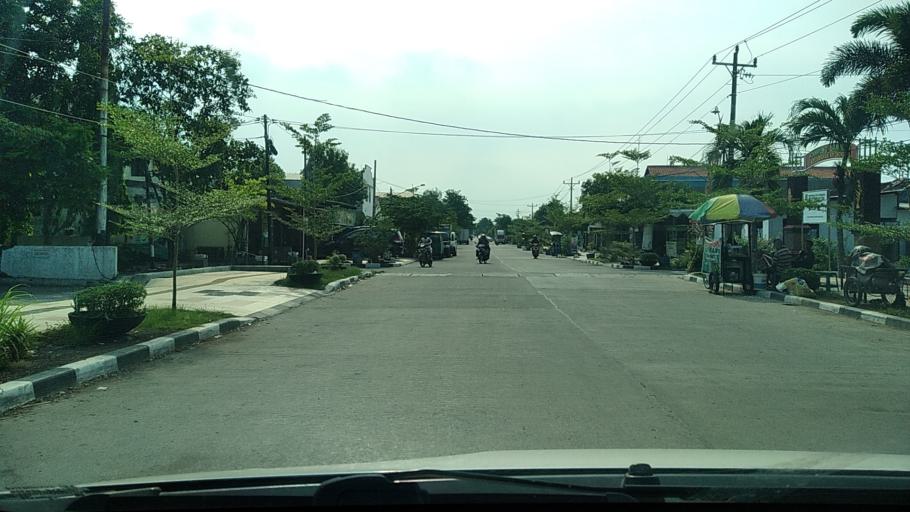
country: ID
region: Central Java
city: Semarang
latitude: -6.9733
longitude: 110.3987
